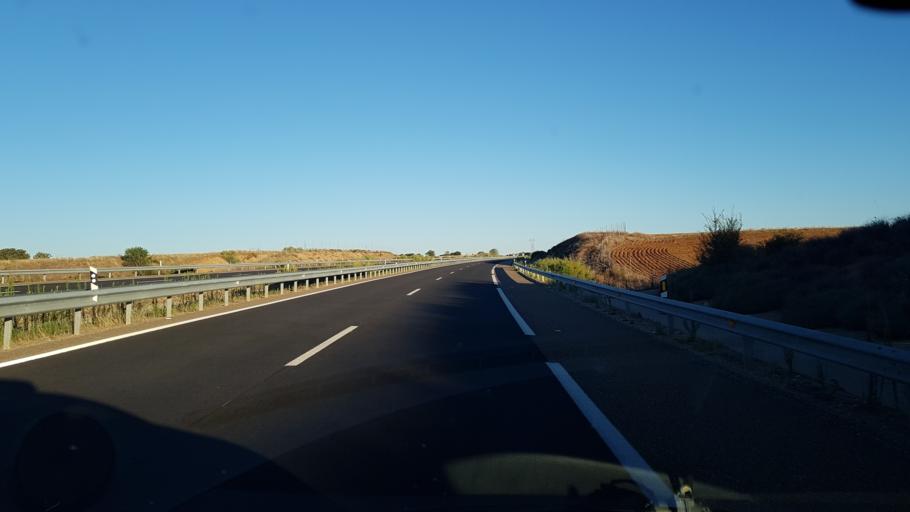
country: ES
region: Castille and Leon
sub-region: Provincia de Zamora
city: Toro
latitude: 41.5434
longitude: -5.4160
